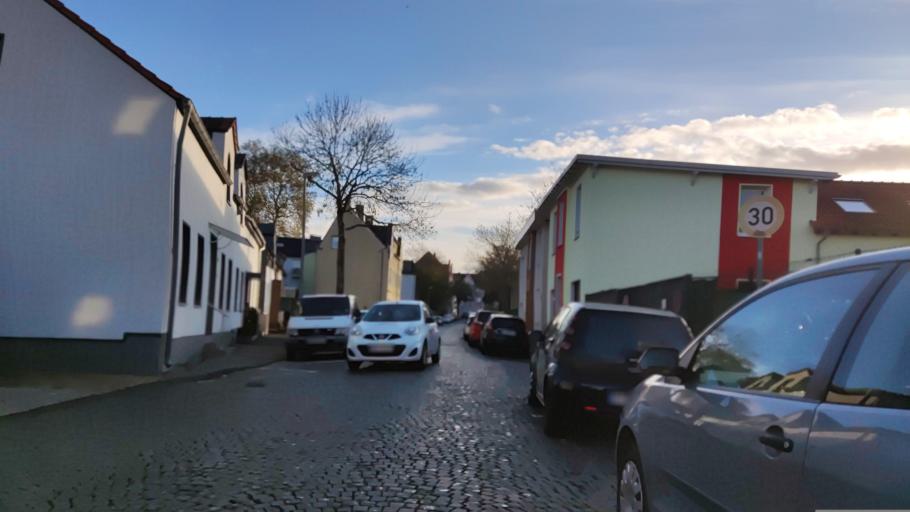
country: DE
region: North Rhine-Westphalia
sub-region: Regierungsbezirk Arnsberg
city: Bochum
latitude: 51.5061
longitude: 7.2087
